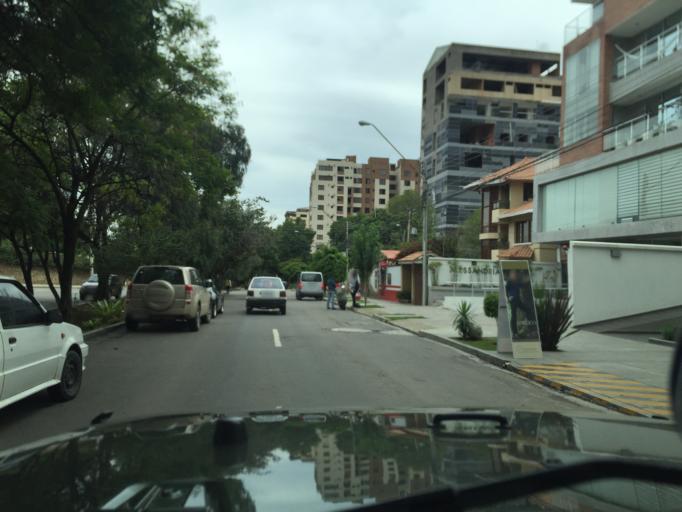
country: BO
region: Cochabamba
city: Cochabamba
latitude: -17.3746
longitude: -66.1497
